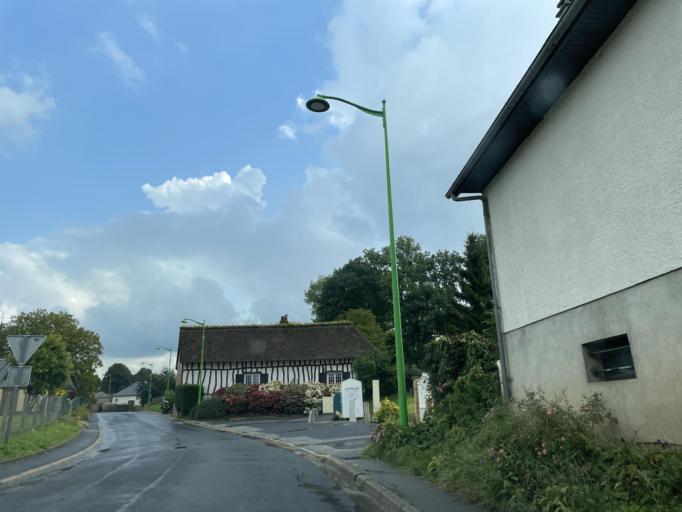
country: FR
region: Haute-Normandie
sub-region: Departement de la Seine-Maritime
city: Saint-Martin-en-Campagne
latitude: 49.9437
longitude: 1.2595
